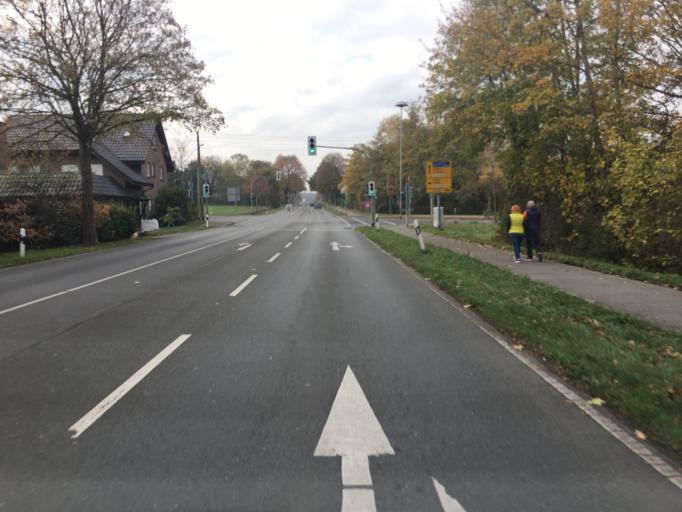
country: DE
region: North Rhine-Westphalia
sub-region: Regierungsbezirk Dusseldorf
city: Xanten
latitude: 51.6542
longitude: 6.4589
